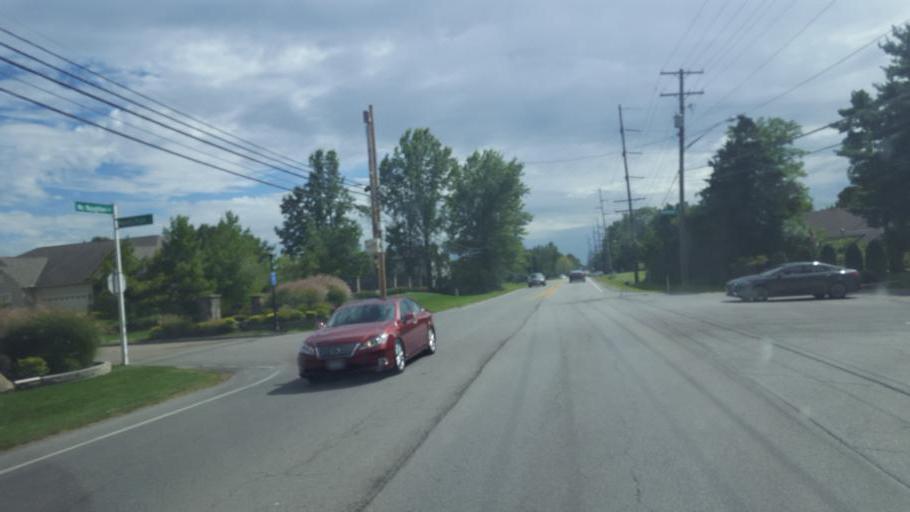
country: US
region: Ohio
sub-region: Franklin County
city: Reynoldsburg
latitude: 39.9731
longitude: -82.8368
